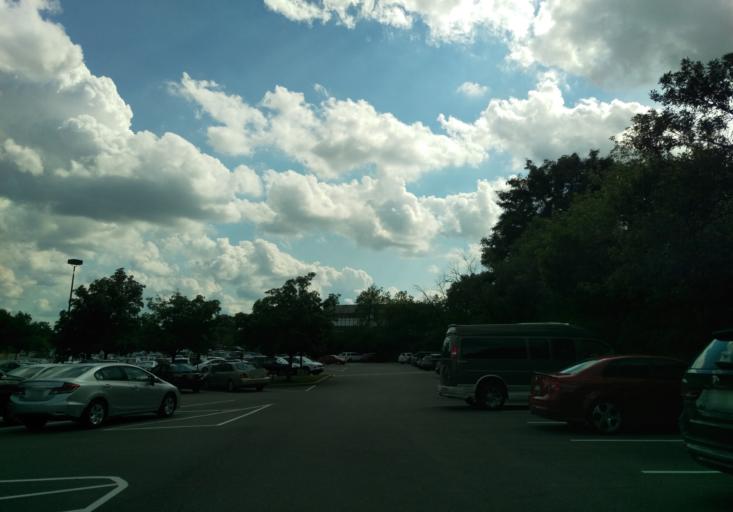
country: US
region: Wisconsin
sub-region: Dane County
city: Shorewood Hills
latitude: 43.0733
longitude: -89.4543
